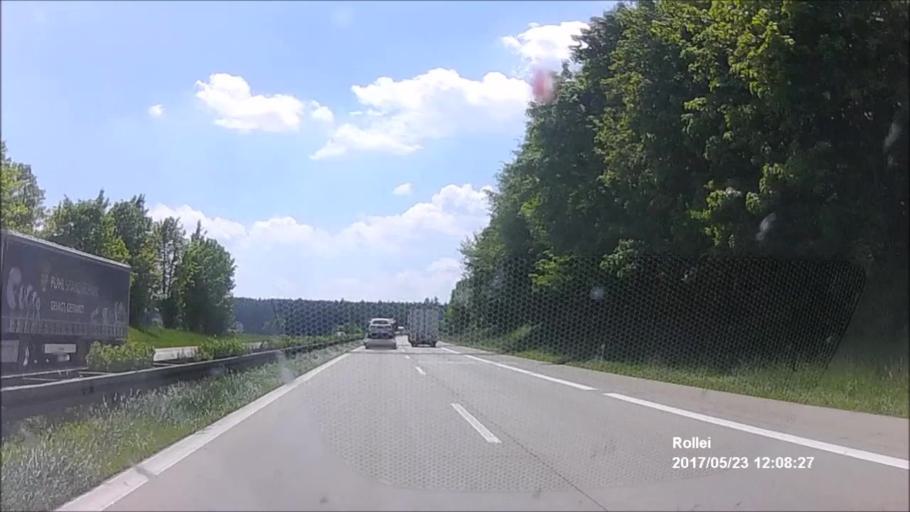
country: DE
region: Bavaria
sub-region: Lower Bavaria
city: Bad Abbach
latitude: 48.9158
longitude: 12.0881
